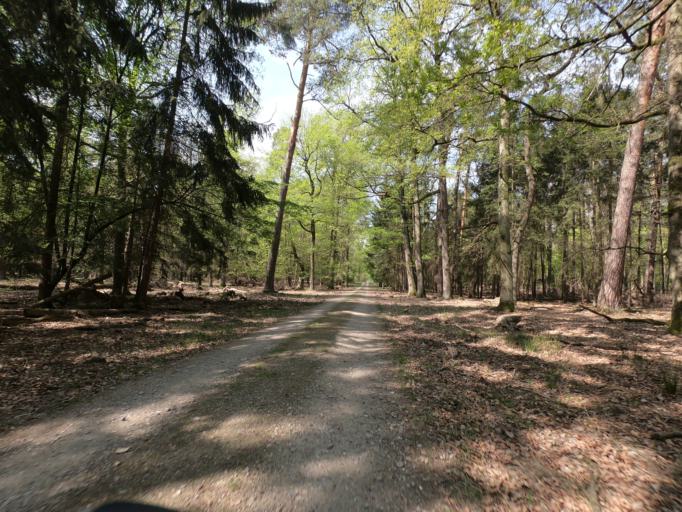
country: DE
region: Hesse
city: Kelsterbach
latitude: 50.0190
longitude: 8.5375
